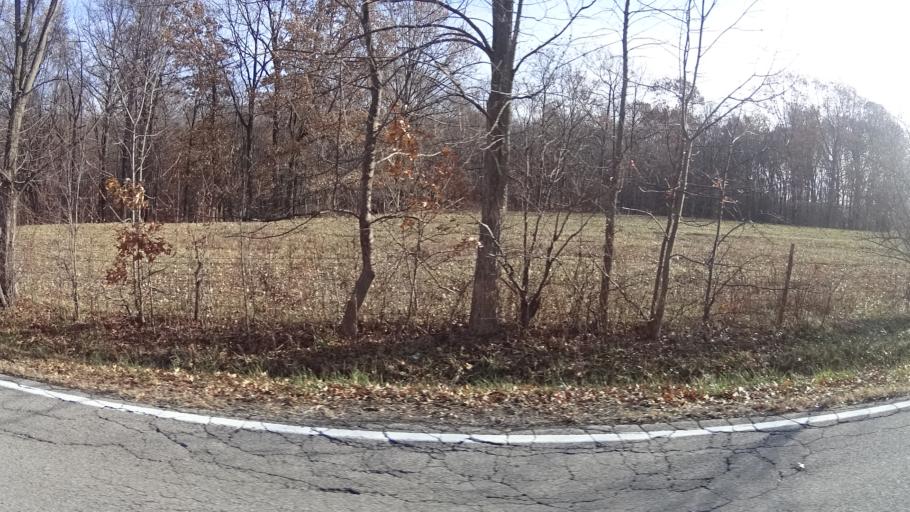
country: US
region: Ohio
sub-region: Lorain County
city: Grafton
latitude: 41.2130
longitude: -82.0433
